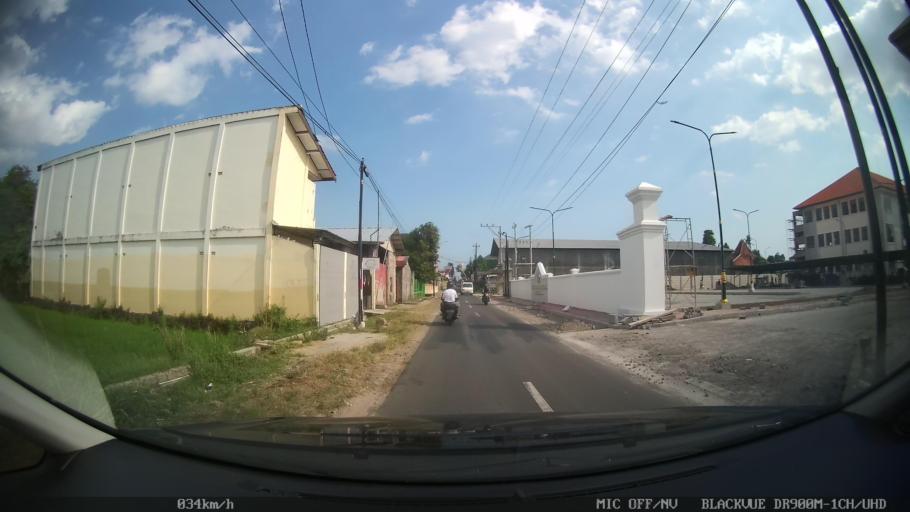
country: ID
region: Daerah Istimewa Yogyakarta
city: Gamping Lor
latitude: -7.7963
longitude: 110.3363
